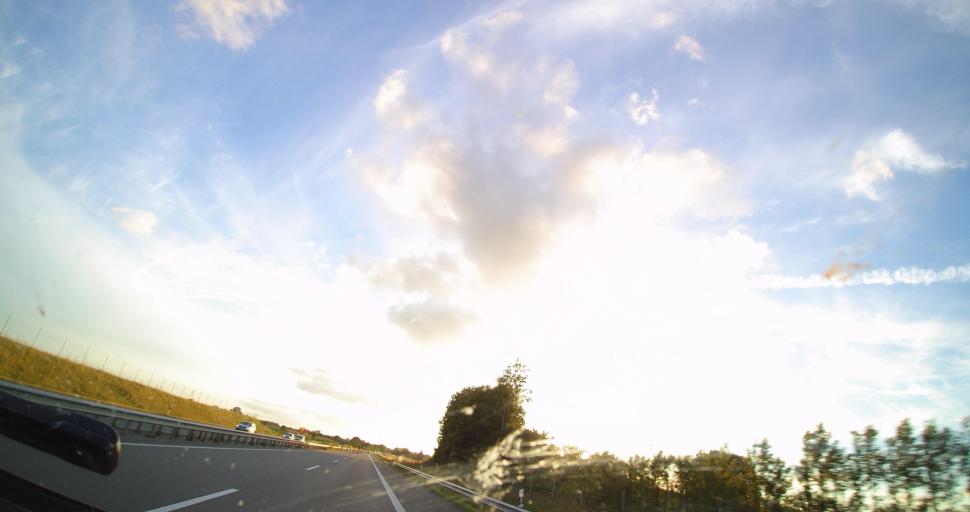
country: DE
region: Schleswig-Holstein
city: Weede
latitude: 53.9199
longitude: 10.3515
